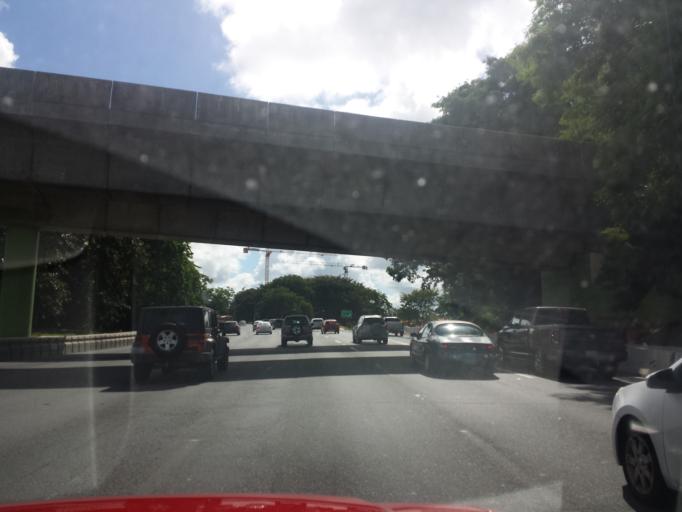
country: PR
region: Guaynabo
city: Guaynabo
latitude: 18.3909
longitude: -66.0718
